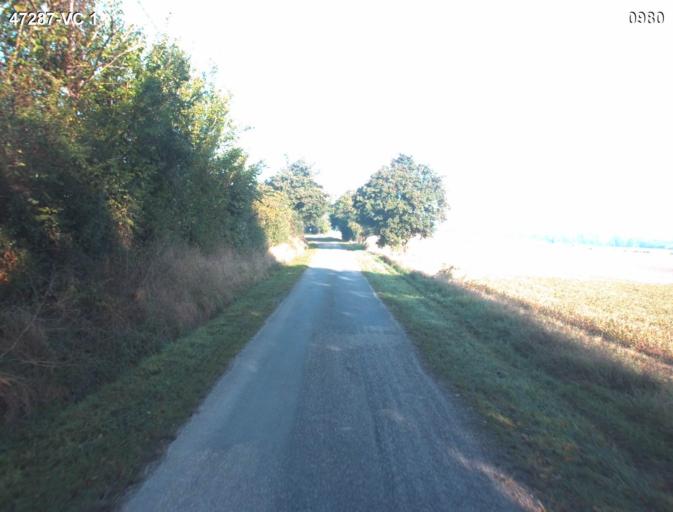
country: FR
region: Aquitaine
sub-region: Departement du Lot-et-Garonne
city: Sainte-Colombe-en-Bruilhois
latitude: 44.1312
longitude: 0.4531
